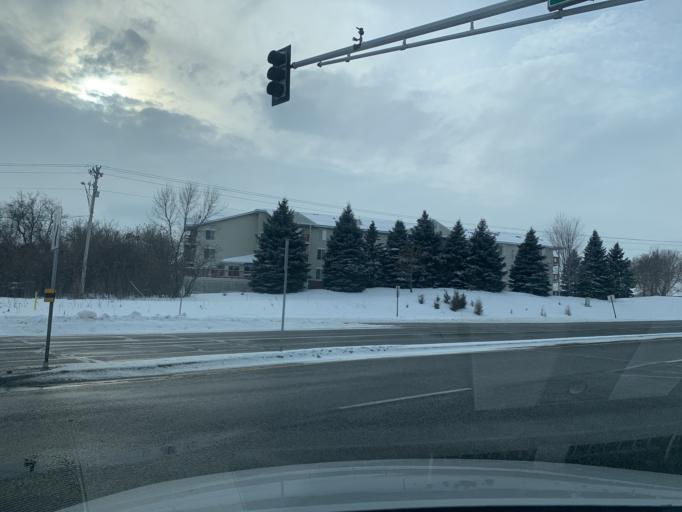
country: US
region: Minnesota
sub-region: Anoka County
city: Anoka
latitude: 45.2317
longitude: -93.4001
